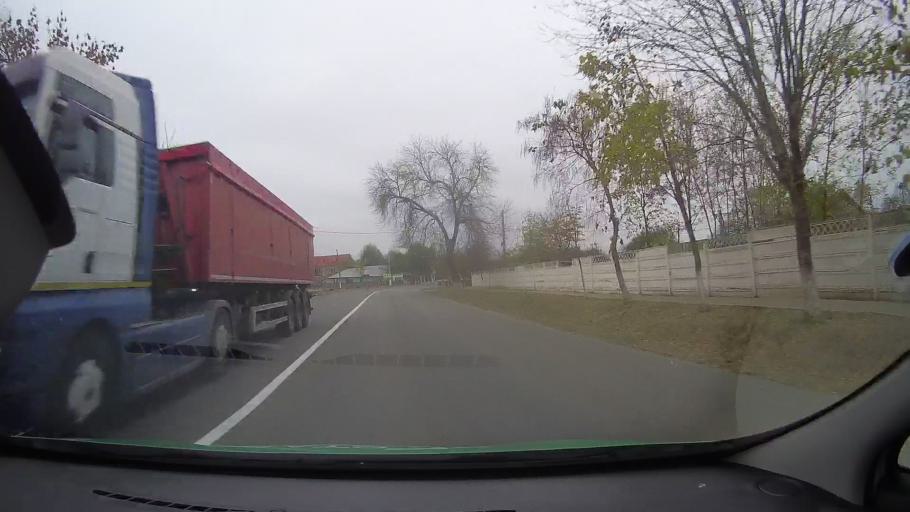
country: RO
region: Ialomita
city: Tandarei
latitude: 44.6407
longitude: 27.6745
